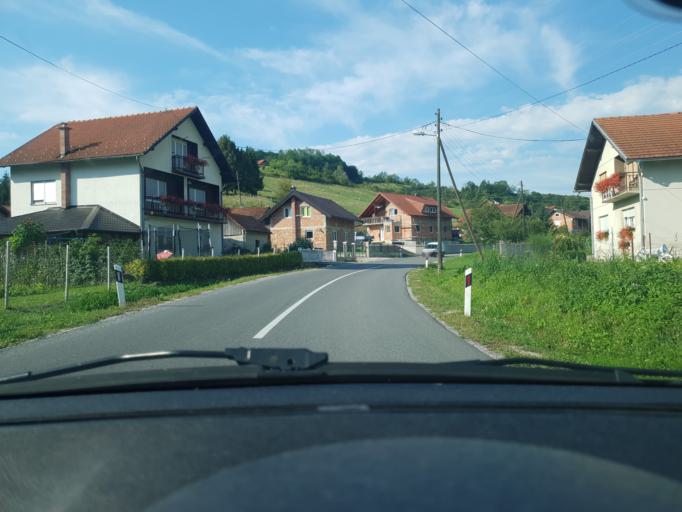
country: HR
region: Krapinsko-Zagorska
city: Pregrada
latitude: 46.0844
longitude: 15.8112
